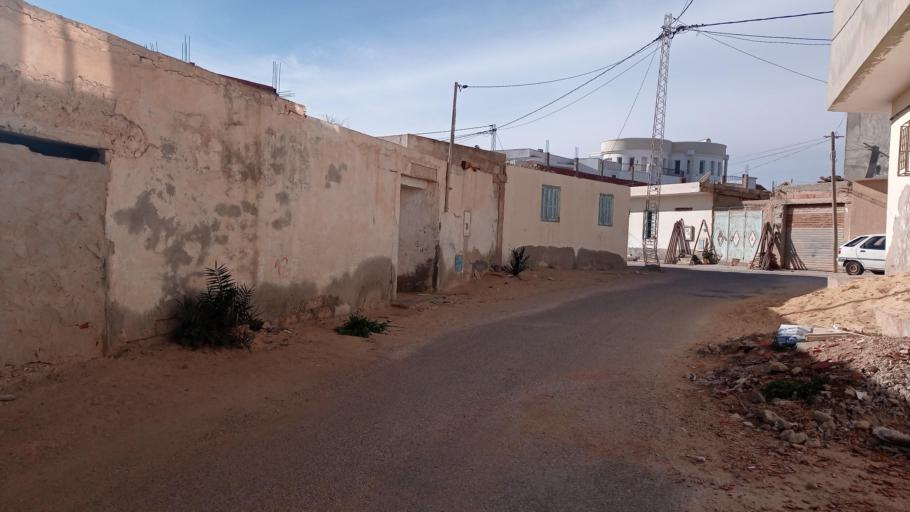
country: TN
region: Qabis
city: Gabes
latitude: 33.8474
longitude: 10.1156
